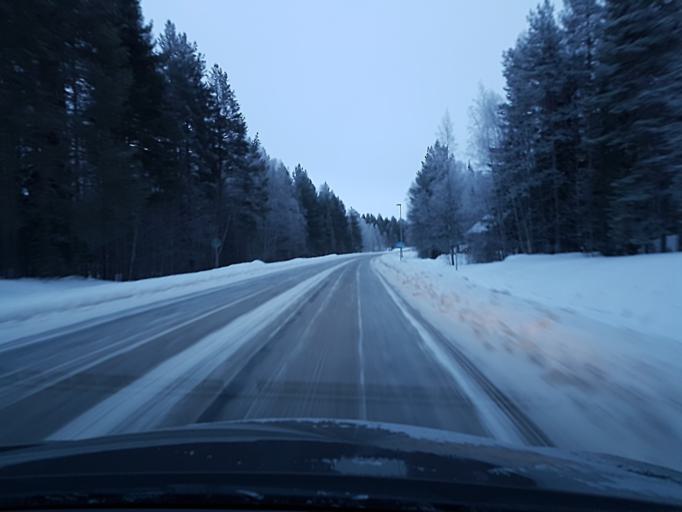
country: SE
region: Norrbotten
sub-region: Pitea Kommun
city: Roknas
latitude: 65.3422
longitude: 21.1415
